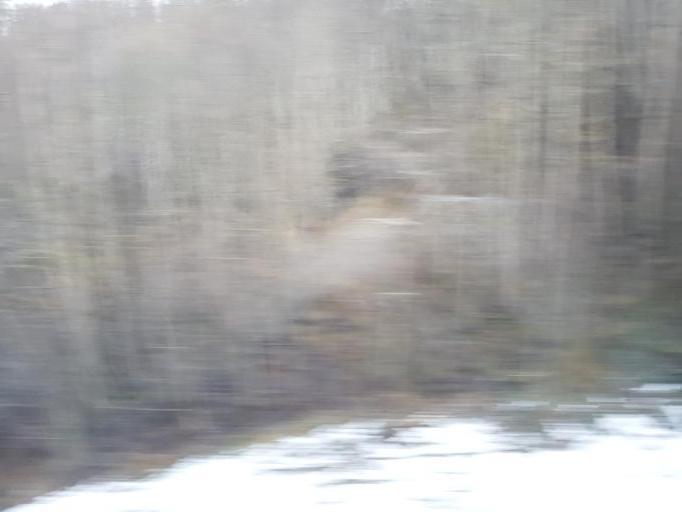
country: NO
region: Sor-Trondelag
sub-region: Midtre Gauldal
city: Storen
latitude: 62.9758
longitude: 10.2209
